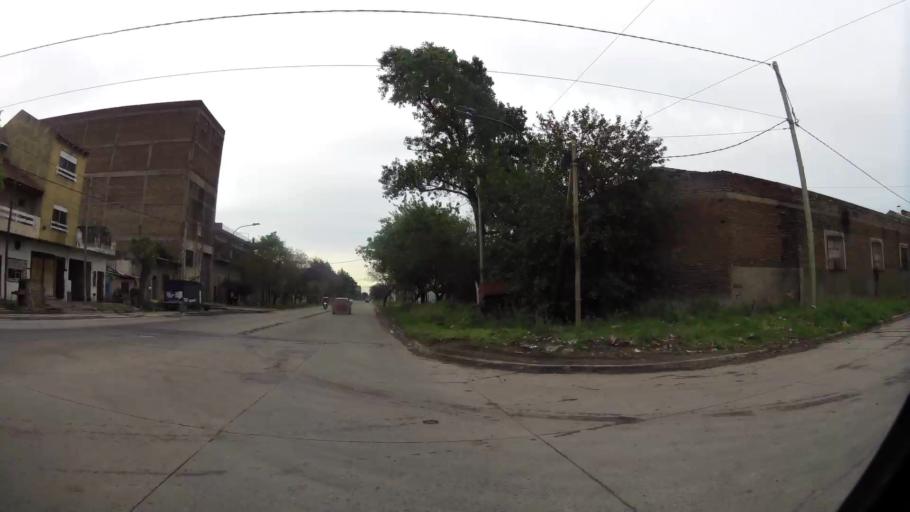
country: AR
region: Buenos Aires
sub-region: Partido de Lanus
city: Lanus
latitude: -34.7135
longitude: -58.3619
